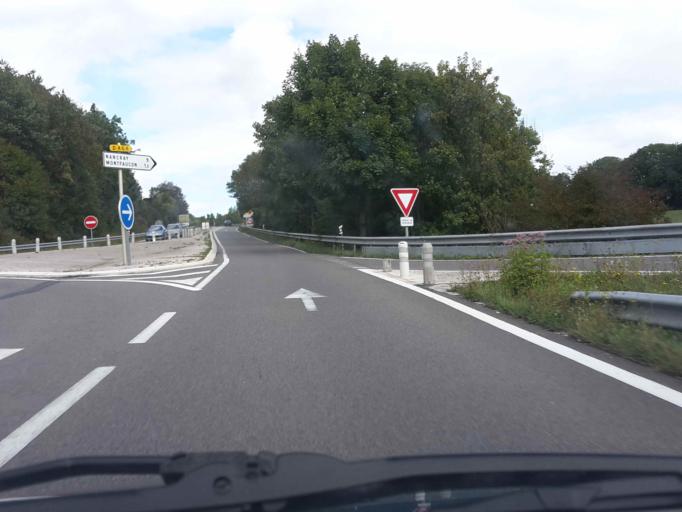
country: FR
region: Franche-Comte
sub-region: Departement du Doubs
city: Morre
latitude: 47.2241
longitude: 6.0778
